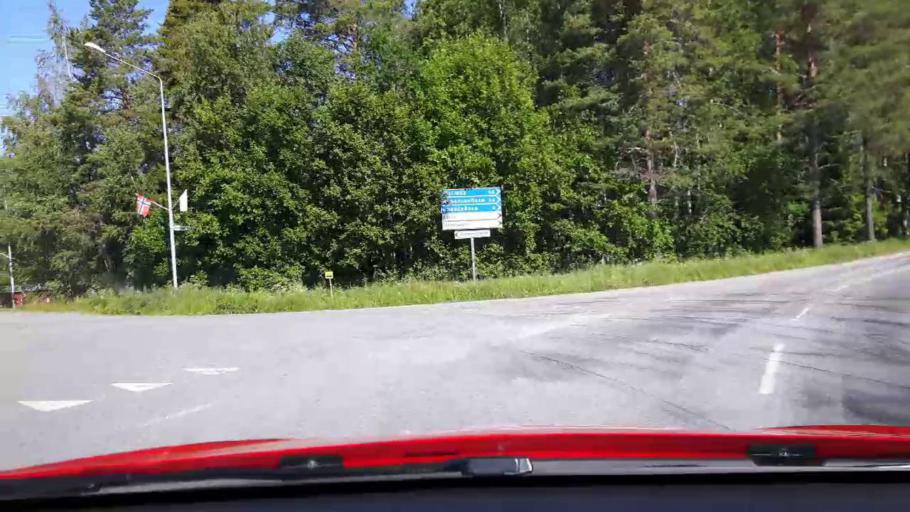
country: SE
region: Jaemtland
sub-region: OEstersunds Kommun
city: Lit
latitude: 63.3906
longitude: 14.9071
